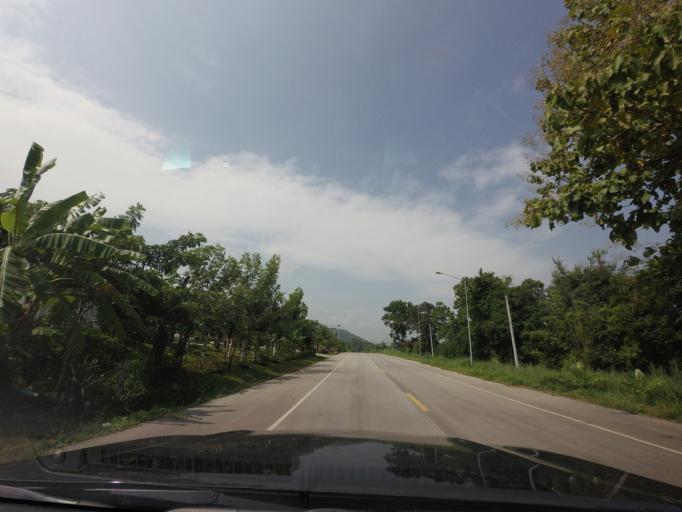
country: LA
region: Xiagnabouli
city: Muang Kenthao
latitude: 17.6834
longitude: 101.3868
